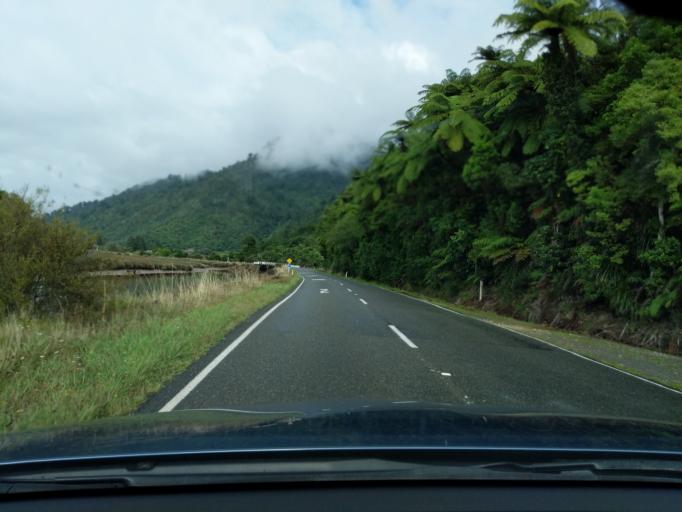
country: NZ
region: Tasman
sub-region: Tasman District
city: Takaka
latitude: -40.6550
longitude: 172.6485
